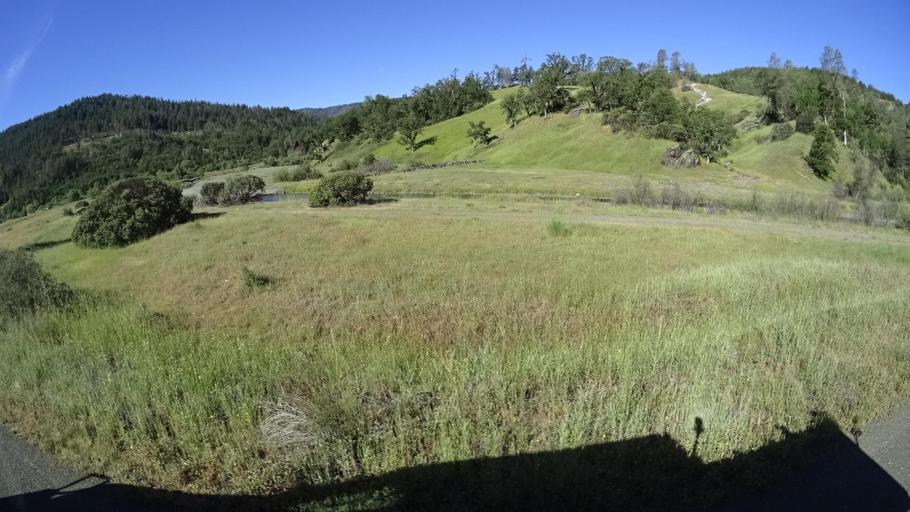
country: US
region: California
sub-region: Lake County
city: Upper Lake
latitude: 39.4152
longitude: -122.9750
